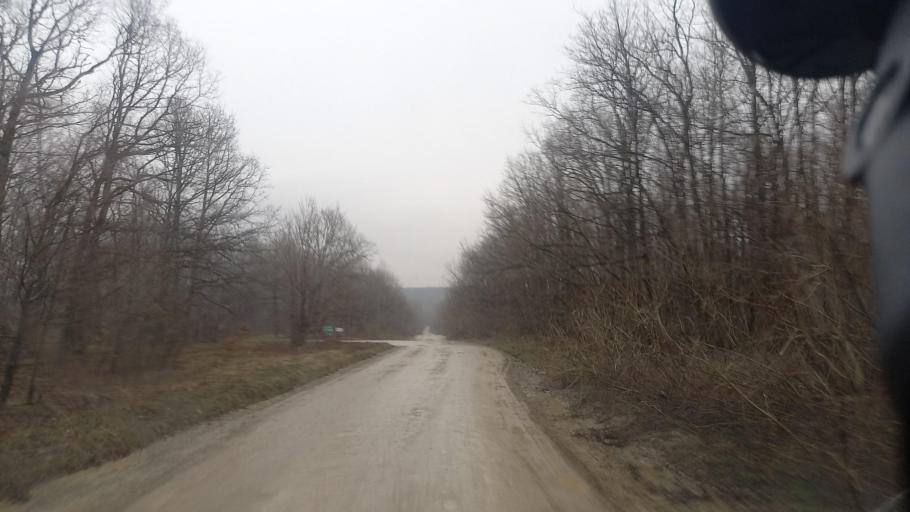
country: RU
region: Krasnodarskiy
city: Saratovskaya
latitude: 44.6635
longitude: 39.2259
